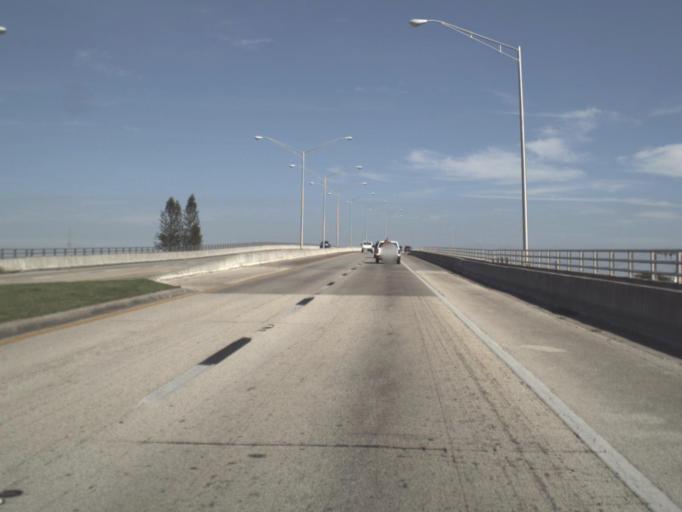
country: US
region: Florida
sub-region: Glades County
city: Moore Haven
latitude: 26.8333
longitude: -81.0928
